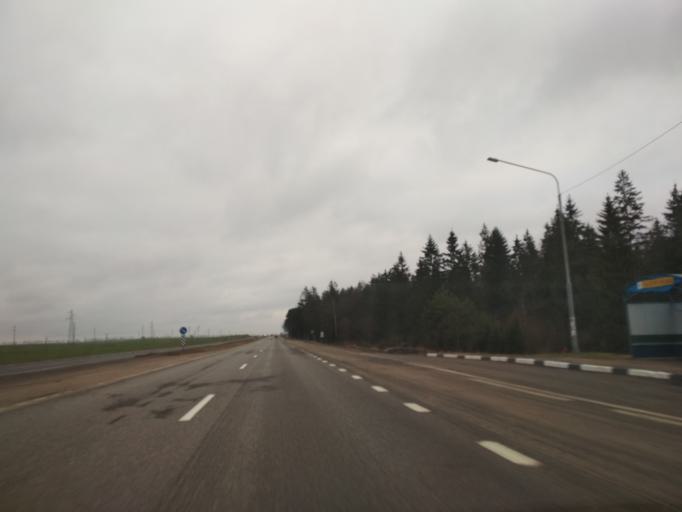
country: BY
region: Minsk
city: Mar''ina Horka
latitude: 53.6104
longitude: 28.0667
